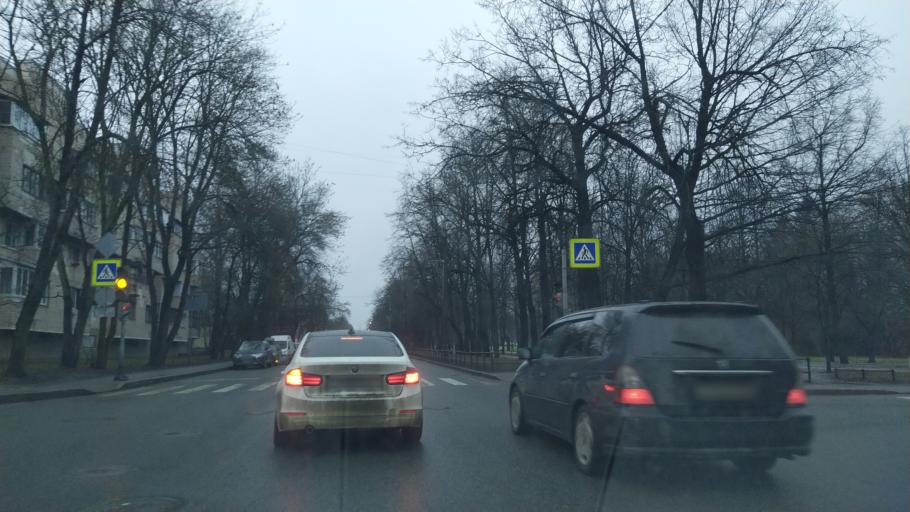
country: RU
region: St.-Petersburg
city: Pushkin
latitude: 59.7251
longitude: 30.4059
